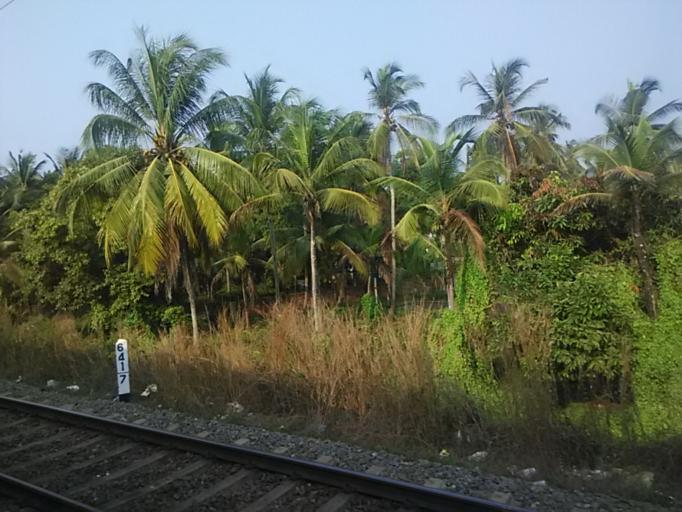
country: IN
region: Kerala
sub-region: Malappuram
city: Pariyapuram
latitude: 11.0641
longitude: 75.8558
